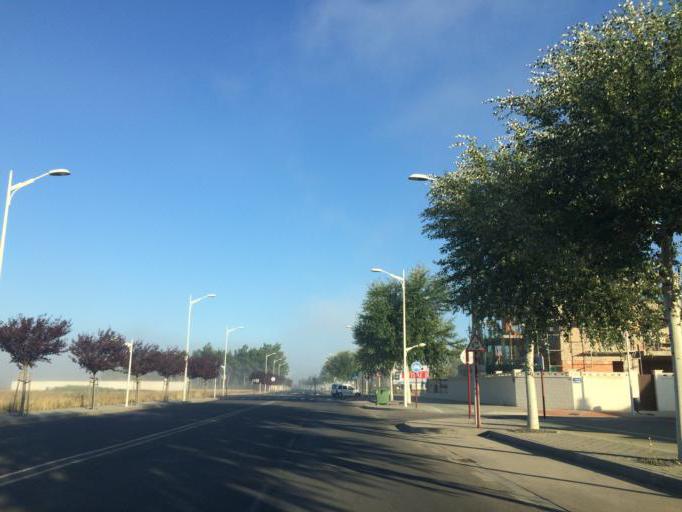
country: ES
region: Castille-La Mancha
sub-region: Provincia de Albacete
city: Albacete
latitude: 39.0034
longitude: -1.8816
